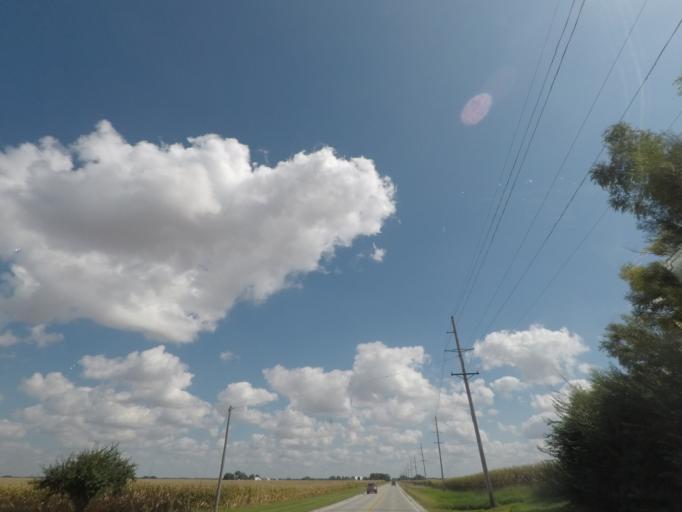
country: US
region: Iowa
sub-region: Story County
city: Nevada
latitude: 42.0227
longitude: -93.4184
